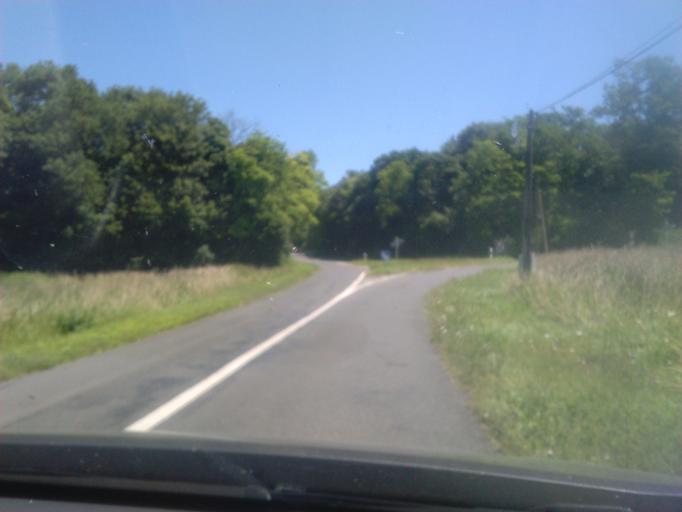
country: FR
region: Centre
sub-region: Departement du Loir-et-Cher
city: Saint-Sulpice-de-Pommeray
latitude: 47.6150
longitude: 1.2261
